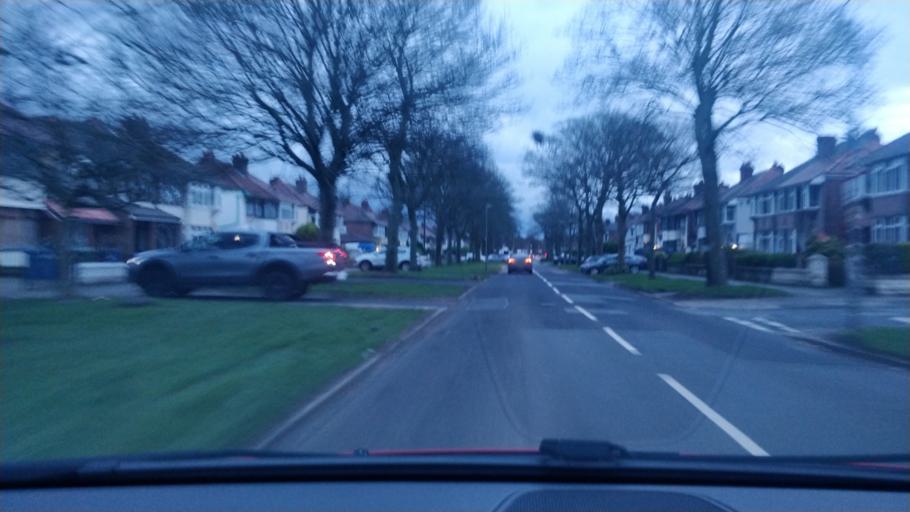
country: GB
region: England
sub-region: Knowsley
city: Knowsley
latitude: 53.4209
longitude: -2.8910
